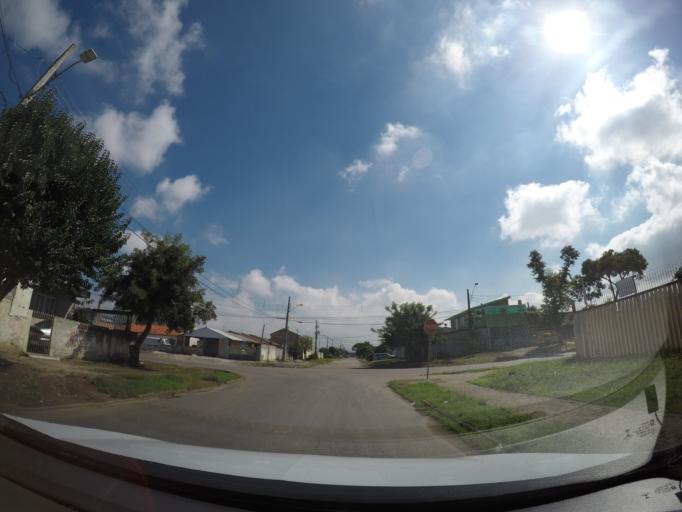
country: BR
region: Parana
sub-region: Sao Jose Dos Pinhais
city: Sao Jose dos Pinhais
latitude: -25.5032
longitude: -49.2164
